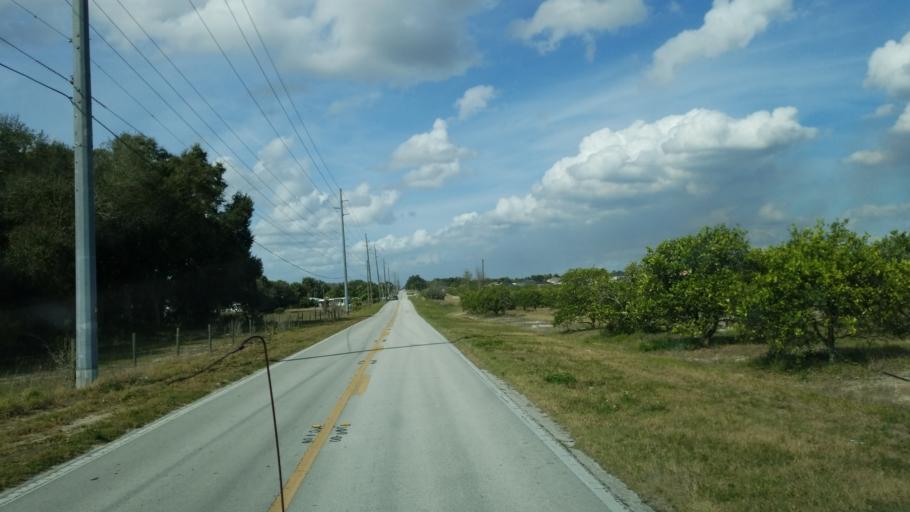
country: US
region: Florida
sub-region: Polk County
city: Davenport
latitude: 28.1370
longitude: -81.5903
